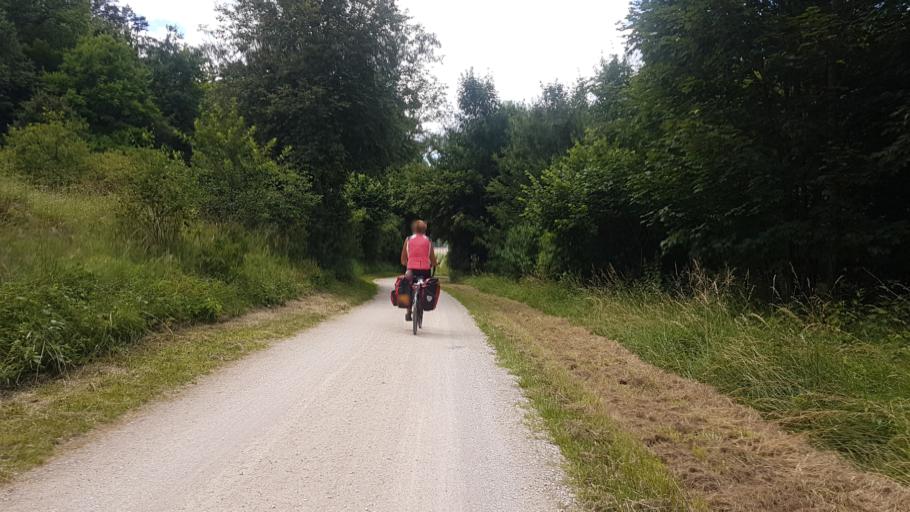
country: DE
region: Bavaria
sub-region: Regierungsbezirk Mittelfranken
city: Solnhofen
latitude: 48.8865
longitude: 11.0285
